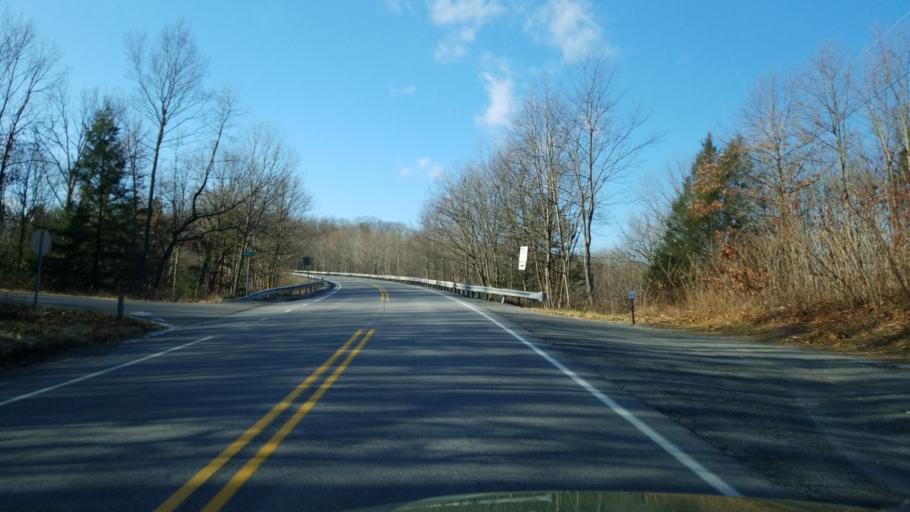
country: US
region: Pennsylvania
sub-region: Clearfield County
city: Hyde
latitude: 41.0005
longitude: -78.4380
